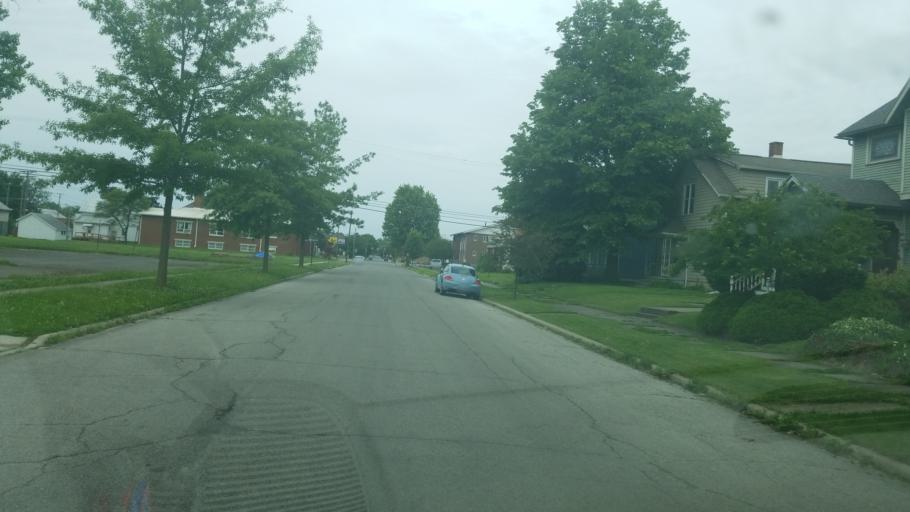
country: US
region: Ohio
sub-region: Crawford County
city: Bucyrus
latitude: 40.8065
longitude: -82.9703
